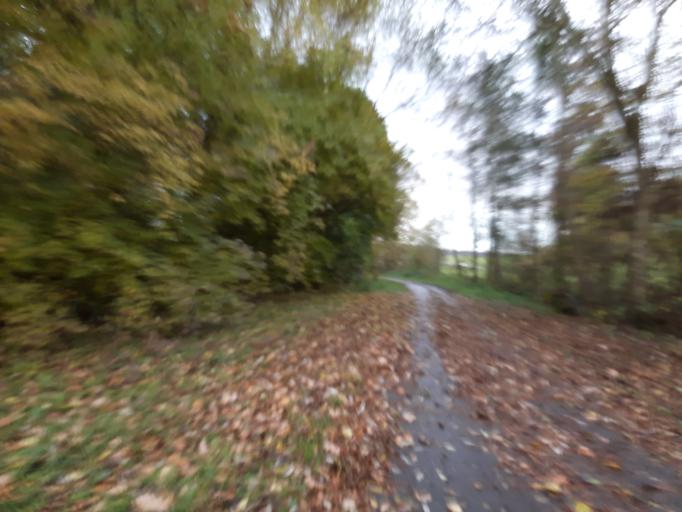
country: DE
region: Baden-Wuerttemberg
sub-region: Regierungsbezirk Stuttgart
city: Eberstadt
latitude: 49.1682
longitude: 9.3046
